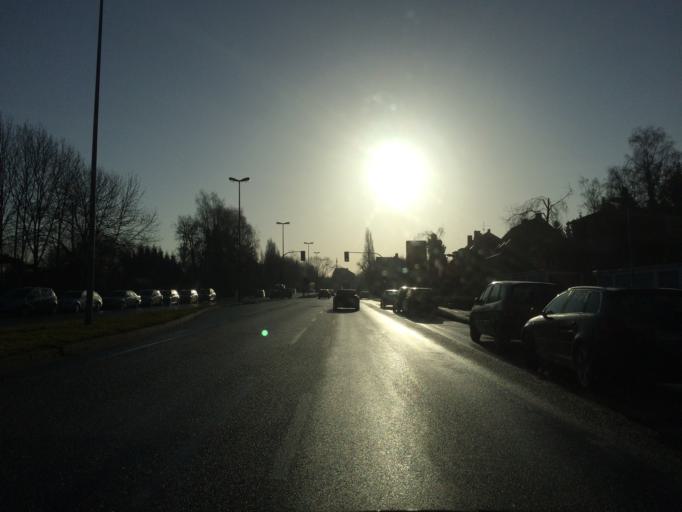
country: DE
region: North Rhine-Westphalia
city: Bochum-Hordel
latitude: 51.5403
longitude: 7.1743
